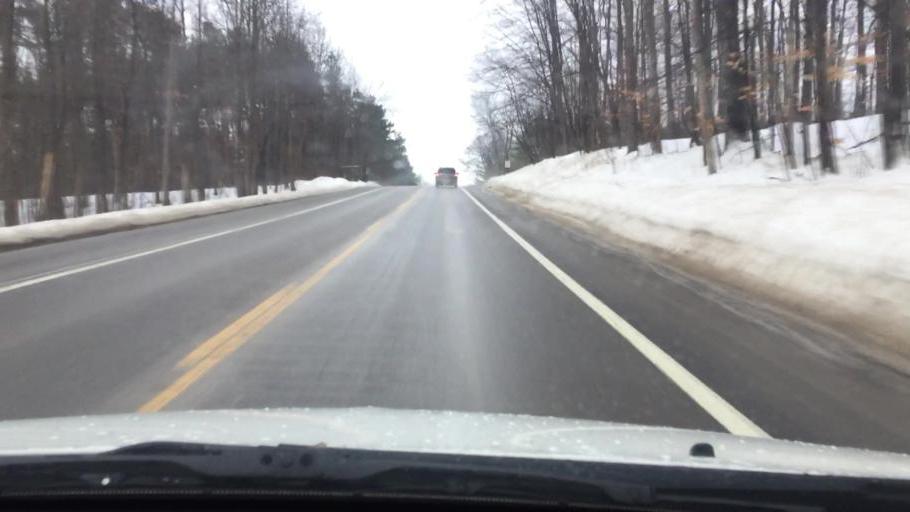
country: US
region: Michigan
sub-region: Charlevoix County
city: East Jordan
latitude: 45.2401
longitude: -85.1812
